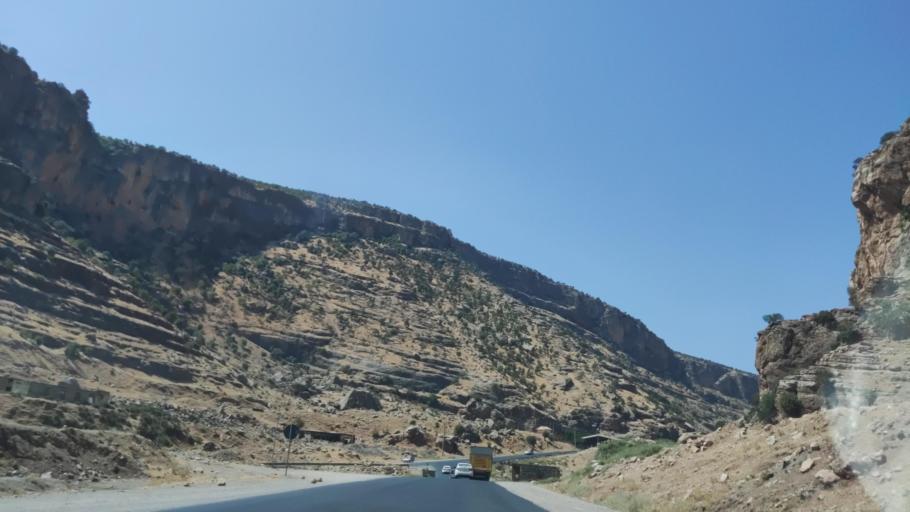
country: IQ
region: Arbil
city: Ruwandiz
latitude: 36.6312
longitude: 44.4431
